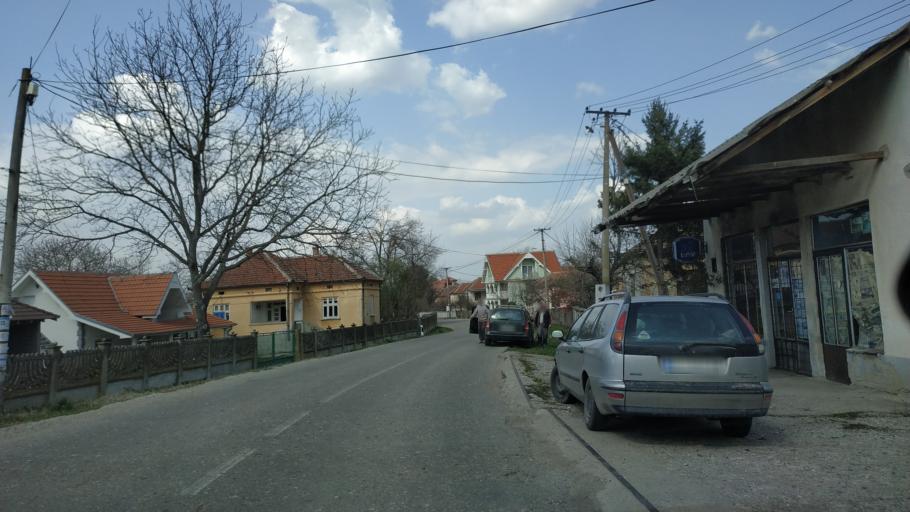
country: RS
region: Central Serbia
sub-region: Nisavski Okrug
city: Razanj
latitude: 43.5771
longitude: 21.5746
